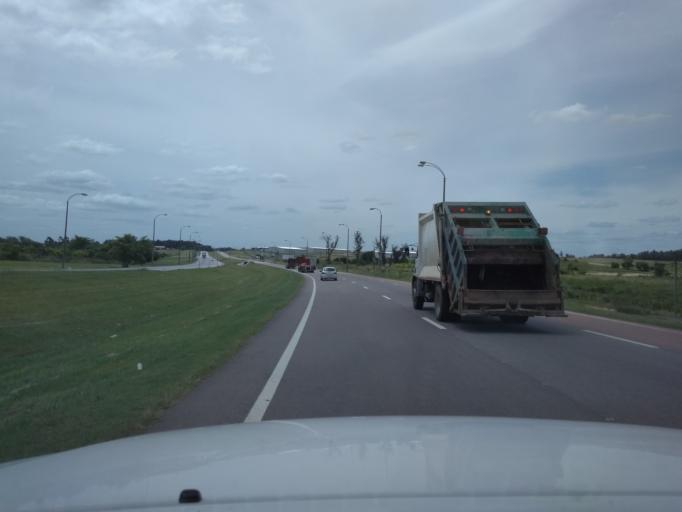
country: UY
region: Canelones
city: Progreso
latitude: -34.6952
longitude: -56.2380
